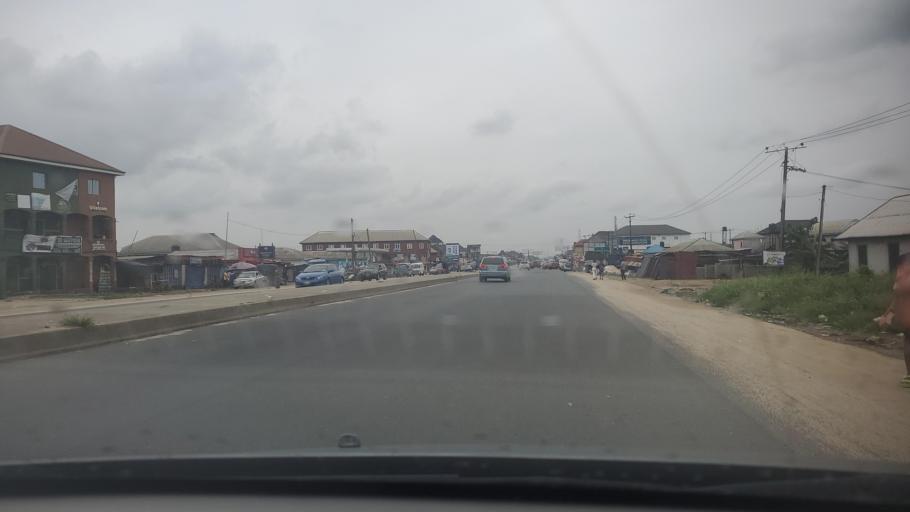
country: NG
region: Rivers
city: Port Harcourt
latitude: 4.8694
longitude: 6.9794
